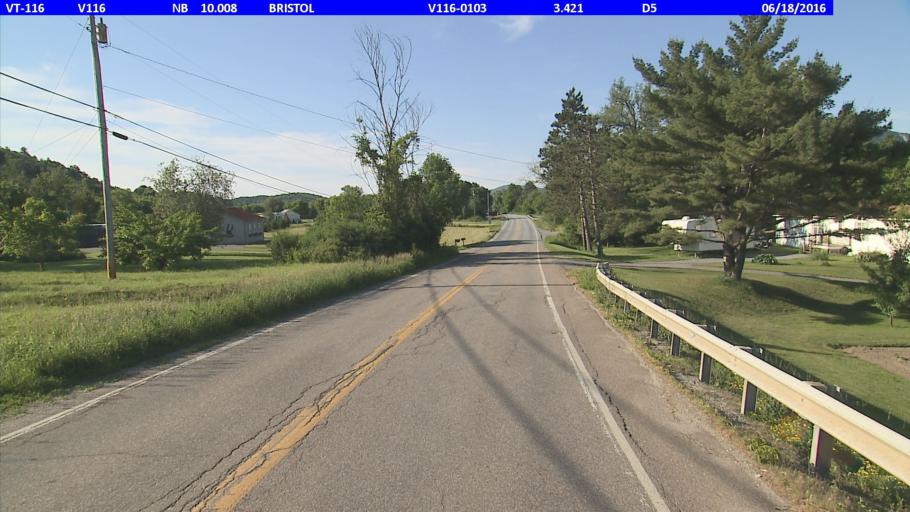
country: US
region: Vermont
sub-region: Addison County
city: Bristol
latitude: 44.0999
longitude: -73.0971
